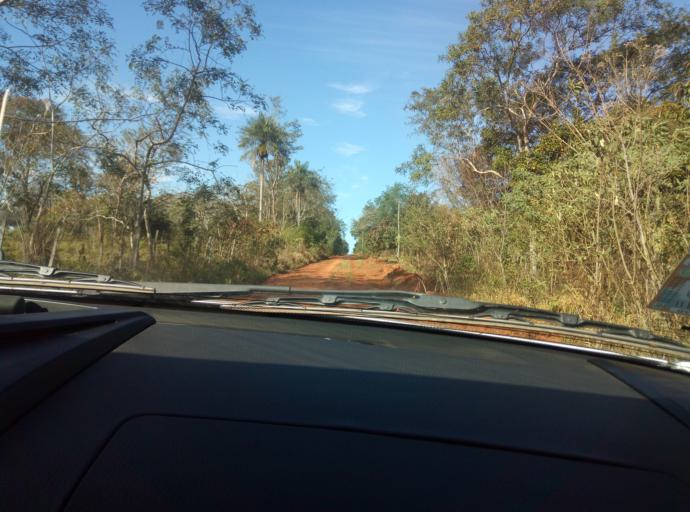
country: PY
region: Caaguazu
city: Carayao
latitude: -25.1703
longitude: -56.2990
